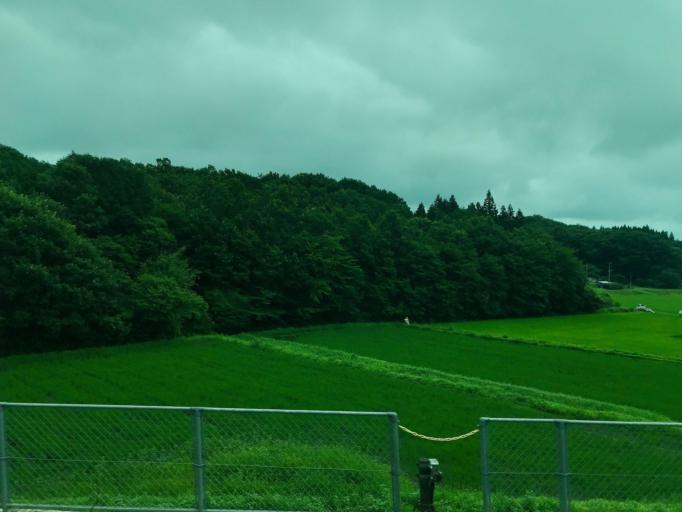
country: JP
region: Tochigi
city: Kuroiso
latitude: 37.0291
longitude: 140.1339
